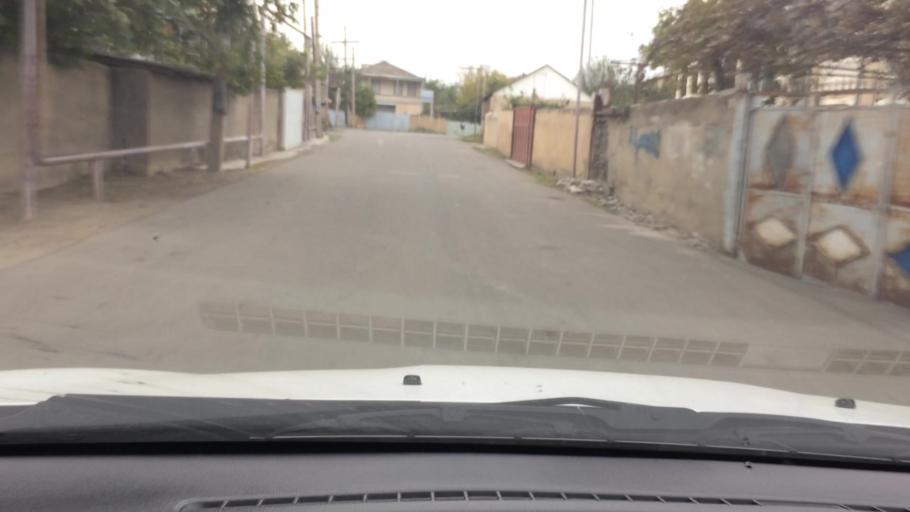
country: GE
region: Kvemo Kartli
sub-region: Marneuli
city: Marneuli
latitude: 41.4809
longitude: 44.7982
